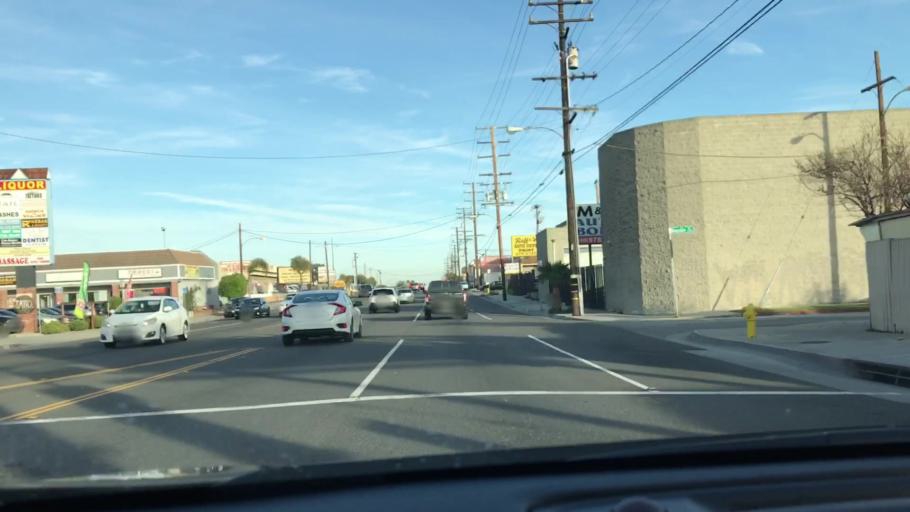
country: US
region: California
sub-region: Los Angeles County
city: Hawthorne
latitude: 33.9019
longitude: -118.3571
